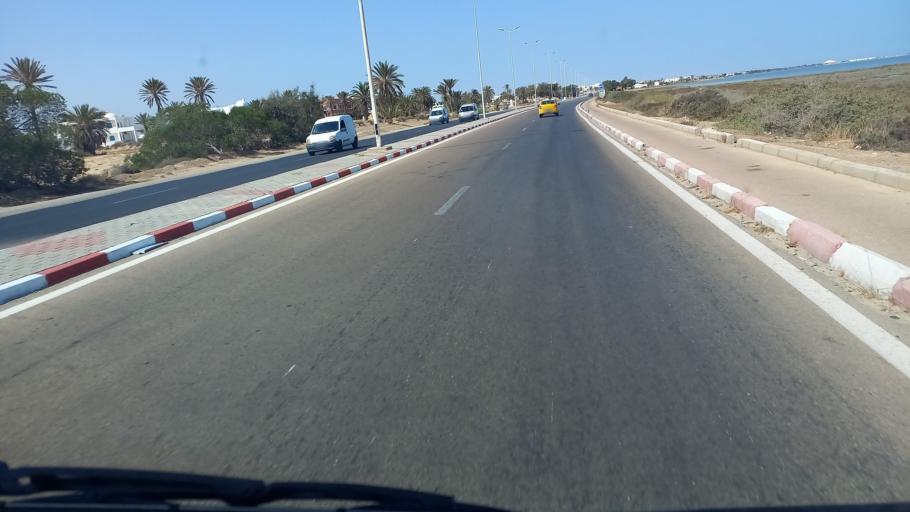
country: TN
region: Madanin
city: Houmt Souk
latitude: 33.8736
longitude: 10.9183
